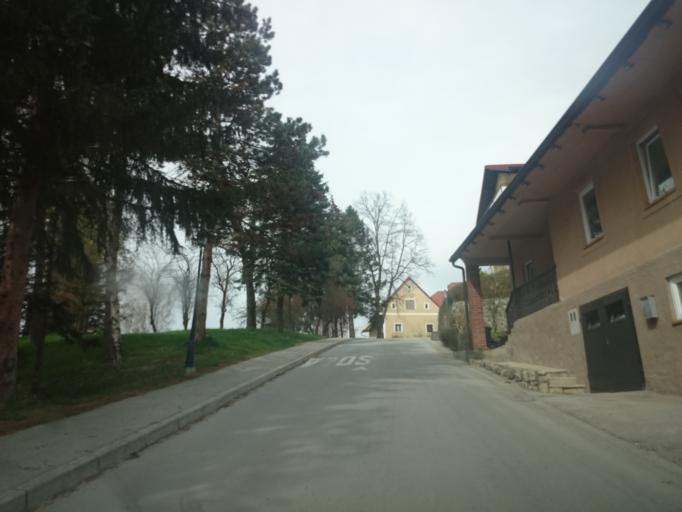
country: SI
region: Sentjur pri Celju
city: Sentjur
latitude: 46.2210
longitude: 15.3960
